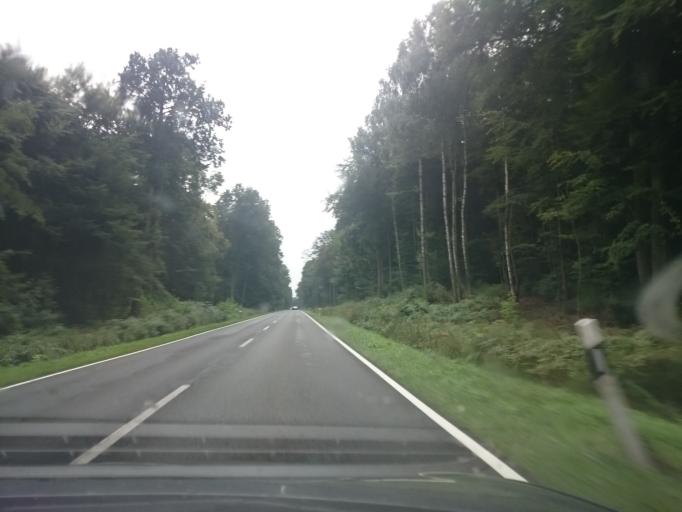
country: DE
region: Brandenburg
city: Gransee
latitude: 53.0663
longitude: 13.1844
